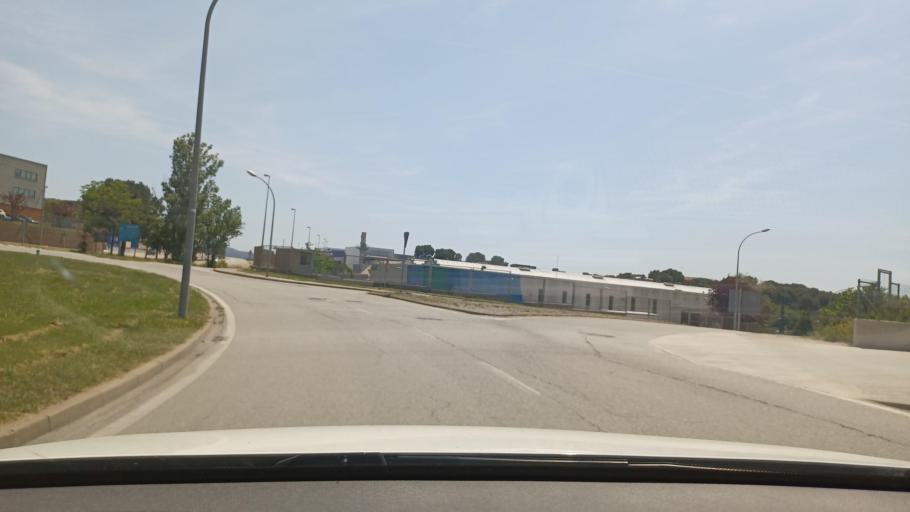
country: ES
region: Catalonia
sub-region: Provincia de Barcelona
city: Barbera del Valles
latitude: 41.5242
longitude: 2.1467
